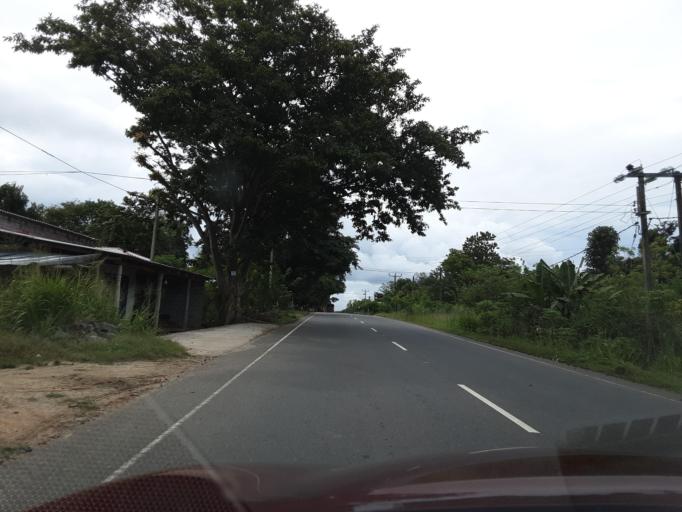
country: LK
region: Uva
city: Badulla
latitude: 7.3895
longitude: 81.1391
